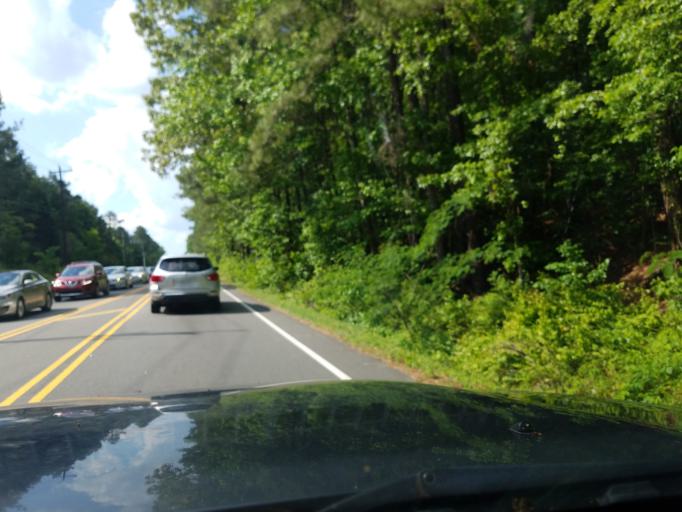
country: US
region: North Carolina
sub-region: Durham County
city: Durham
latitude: 35.9401
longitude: -78.9649
